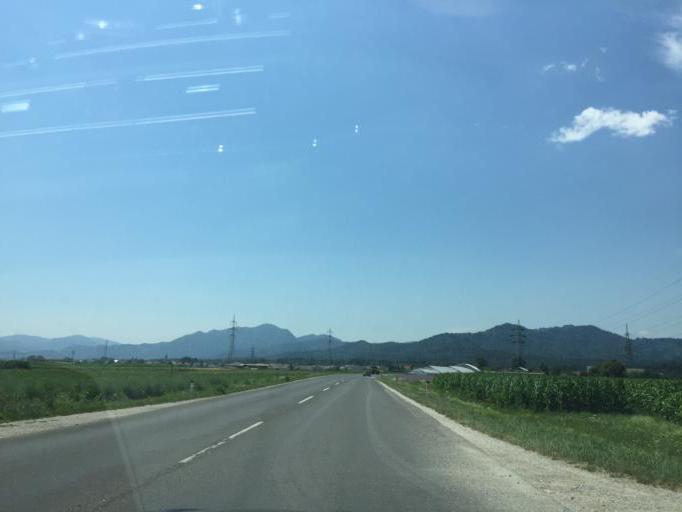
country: SI
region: Kranj
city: Zgornje Bitnje
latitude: 46.2240
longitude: 14.3484
